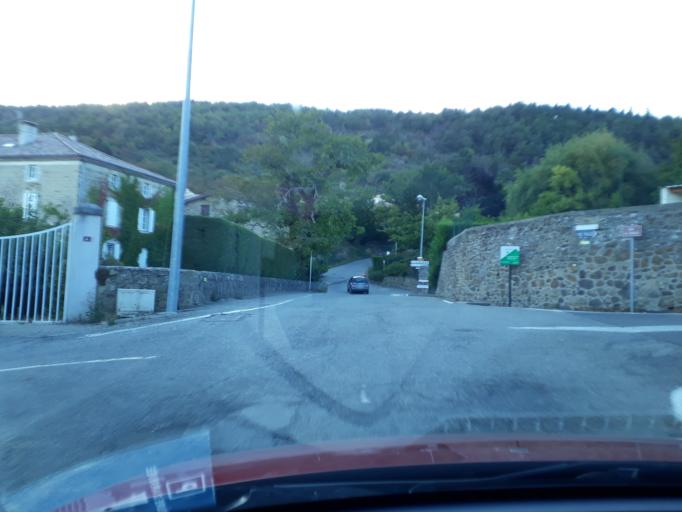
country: FR
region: Rhone-Alpes
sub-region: Departement de l'Ardeche
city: Felines
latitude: 45.3274
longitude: 4.7006
